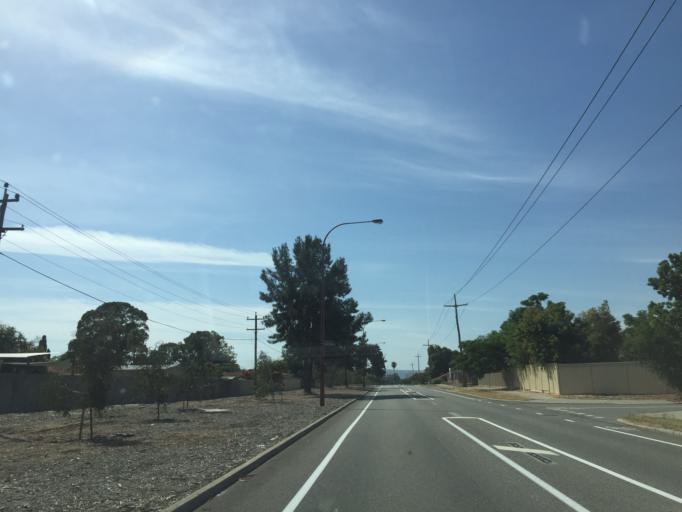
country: AU
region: Western Australia
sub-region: Gosnells
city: Thornlie
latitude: -32.0760
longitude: 115.9622
